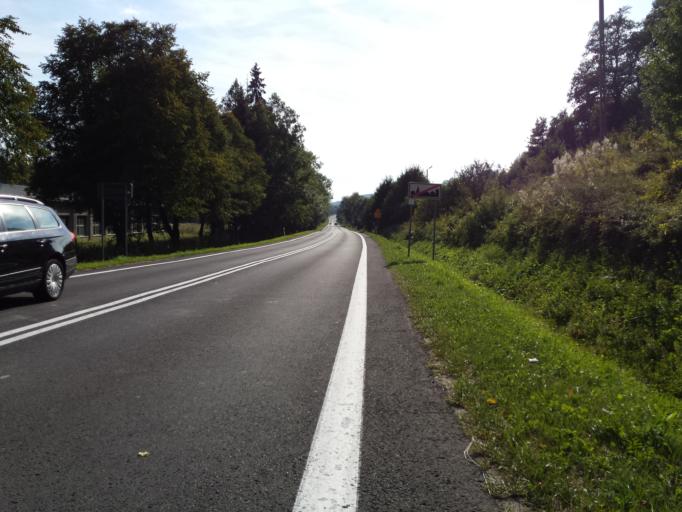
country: PL
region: Subcarpathian Voivodeship
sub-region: Powiat leski
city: Olszanica
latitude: 49.4747
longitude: 22.4312
